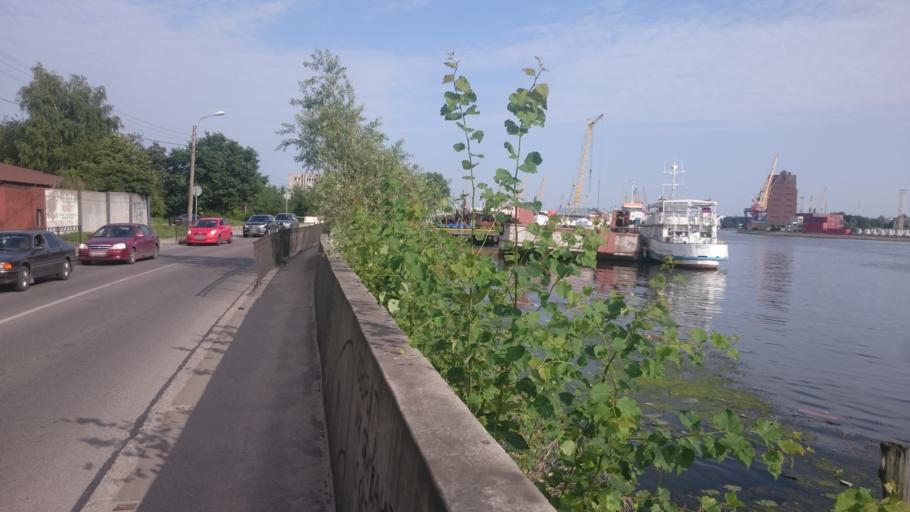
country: RU
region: Kaliningrad
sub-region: Gorod Kaliningrad
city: Kaliningrad
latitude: 54.7080
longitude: 20.4663
